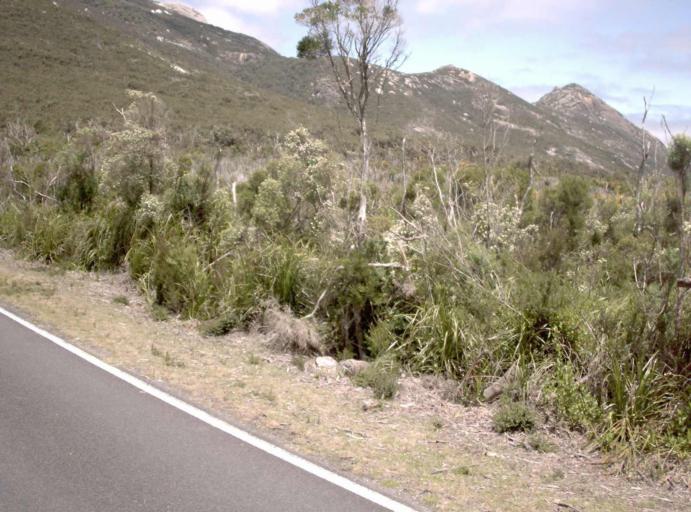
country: AU
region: Victoria
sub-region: Latrobe
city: Morwell
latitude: -39.0263
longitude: 146.3328
